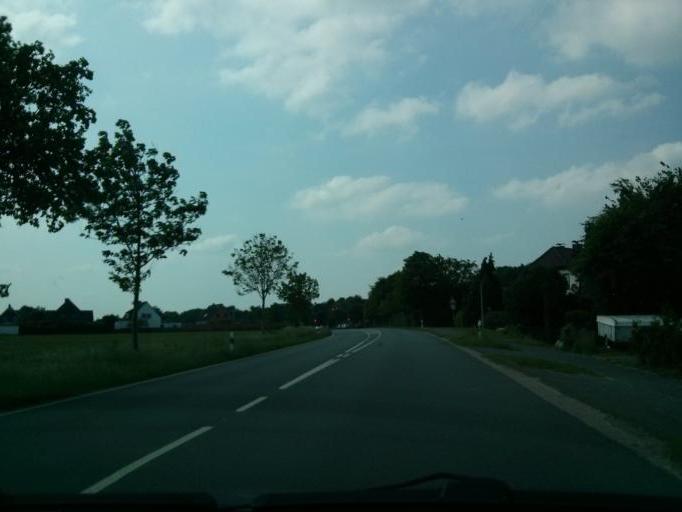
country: DE
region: Lower Saxony
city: Schiffdorf
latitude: 53.5257
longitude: 8.6612
